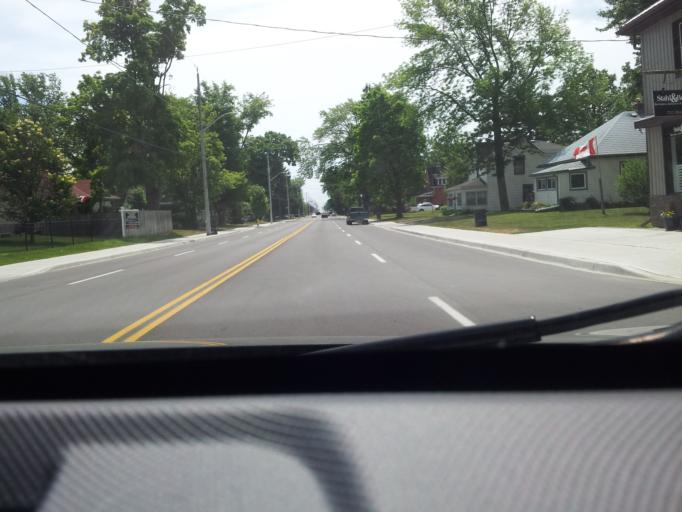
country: CA
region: Ontario
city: Norfolk County
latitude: 42.7921
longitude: -80.2112
